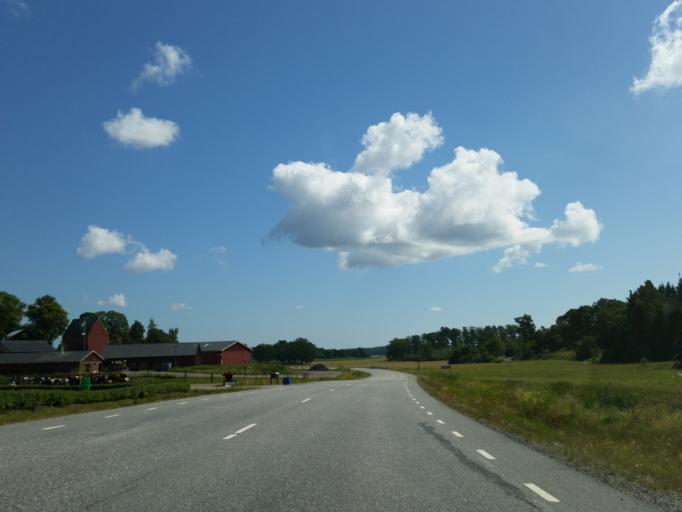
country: SE
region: Soedermanland
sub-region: Trosa Kommun
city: Vagnharad
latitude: 59.0249
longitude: 17.5597
